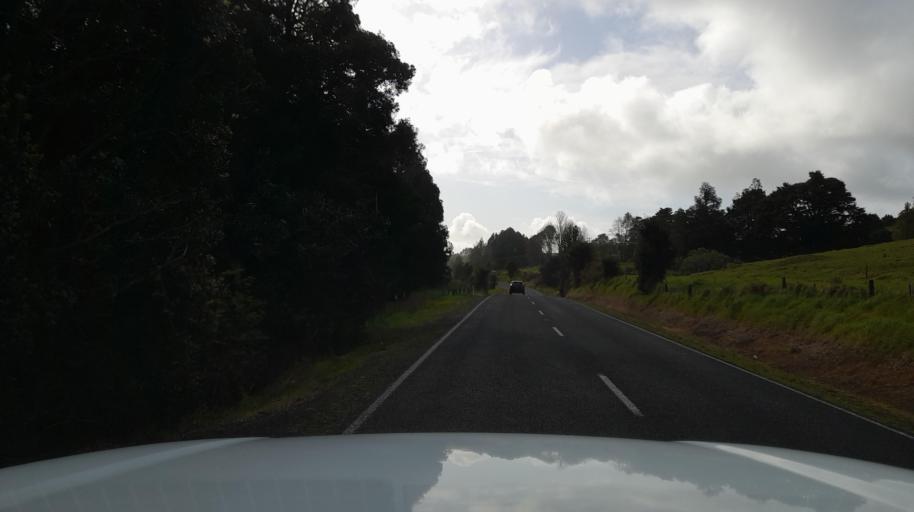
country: NZ
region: Northland
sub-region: Far North District
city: Waimate North
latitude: -35.3603
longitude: 173.8210
